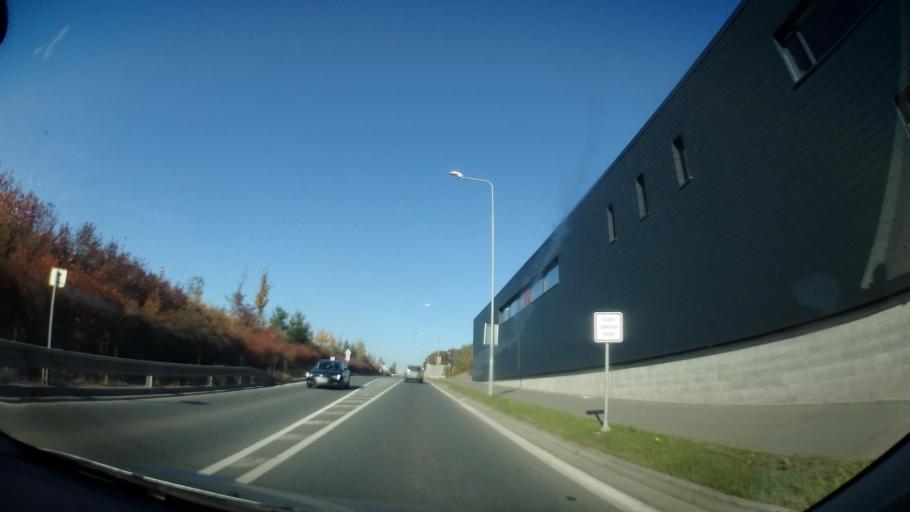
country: CZ
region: Pardubicky
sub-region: Okres Chrudim
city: Chrudim
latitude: 49.9580
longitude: 15.7989
